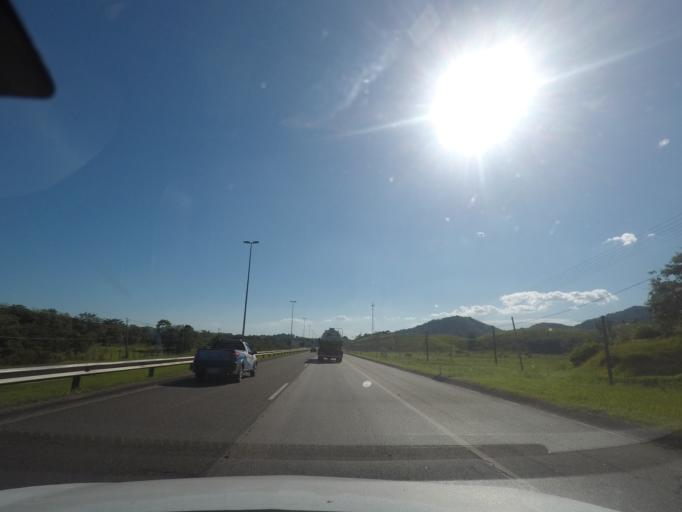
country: BR
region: Rio de Janeiro
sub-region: Guapimirim
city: Guapimirim
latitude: -22.6482
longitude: -43.0733
